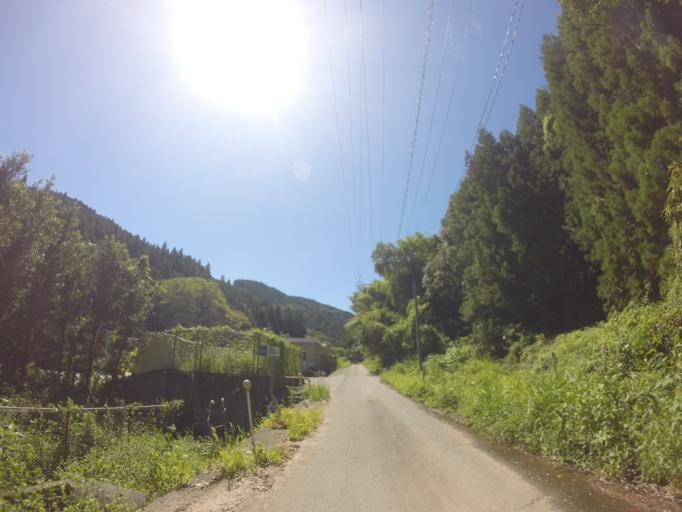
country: JP
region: Shizuoka
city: Shimada
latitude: 34.9114
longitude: 138.1742
